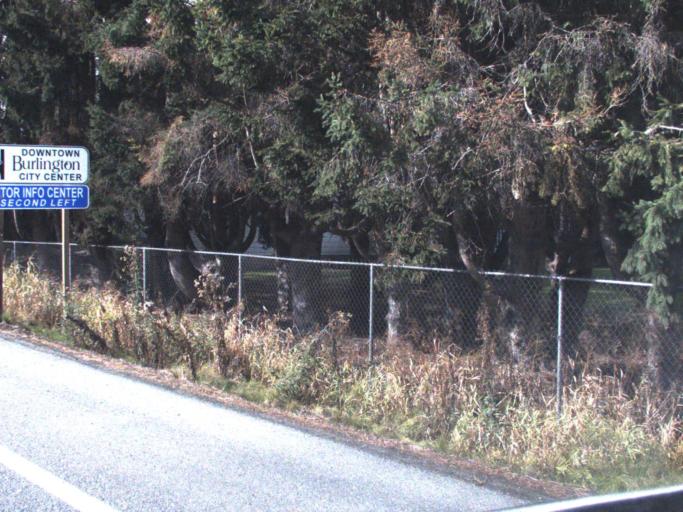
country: US
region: Washington
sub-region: Skagit County
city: Burlington
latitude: 48.4785
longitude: -122.3202
